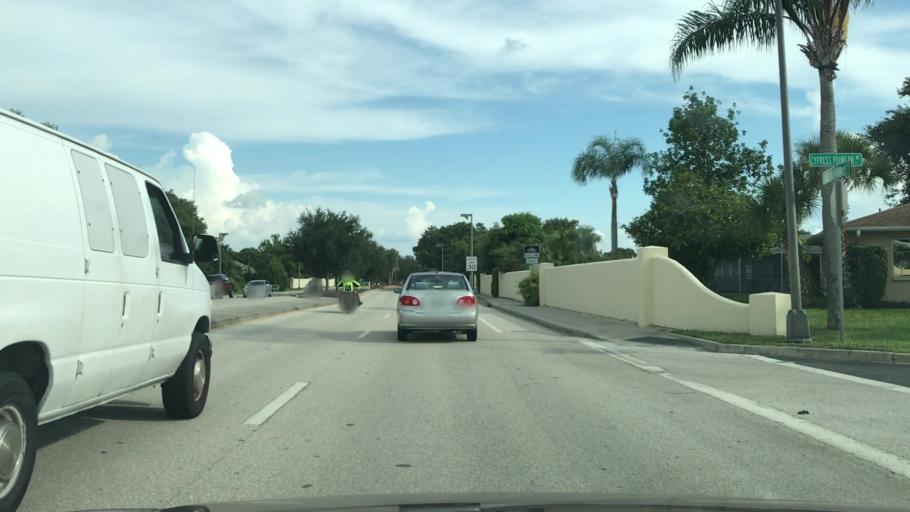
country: US
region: Florida
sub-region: Sarasota County
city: Plantation
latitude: 27.0785
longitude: -82.3890
